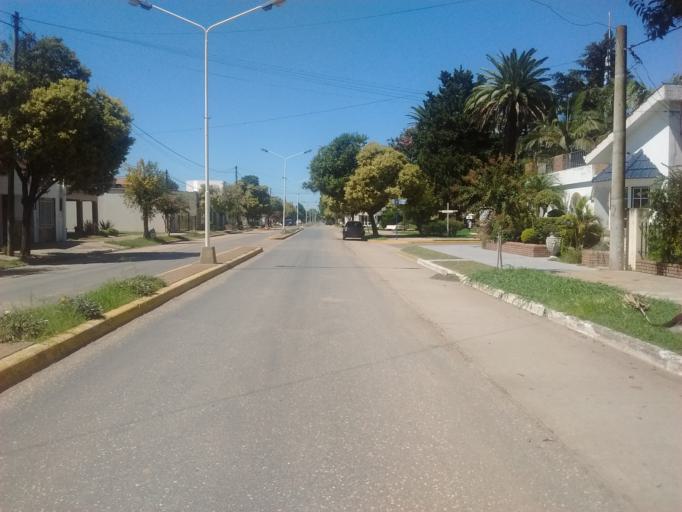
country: AR
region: Santa Fe
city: Galvez
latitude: -31.9046
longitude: -61.2787
